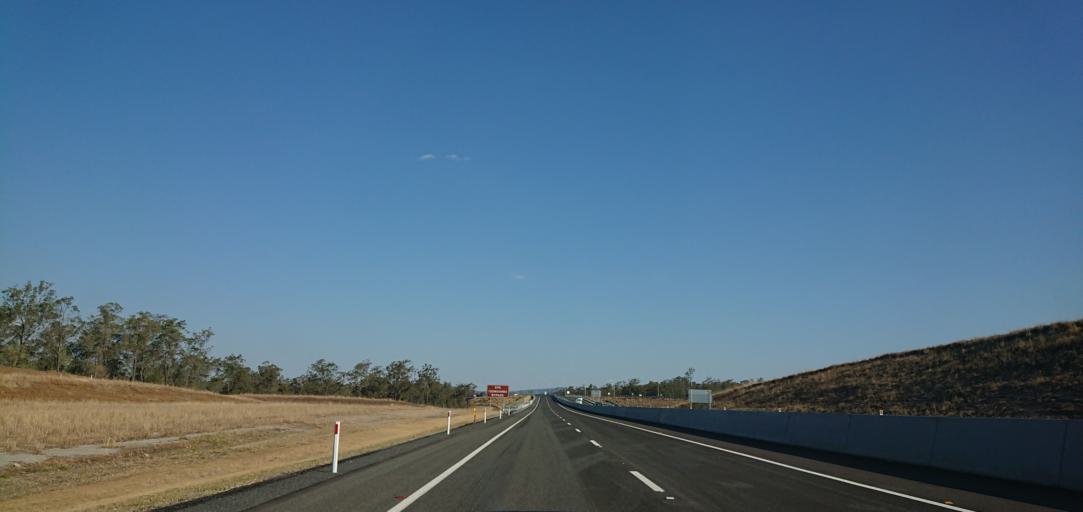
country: AU
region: Queensland
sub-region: Toowoomba
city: Rangeville
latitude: -27.5381
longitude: 152.0770
